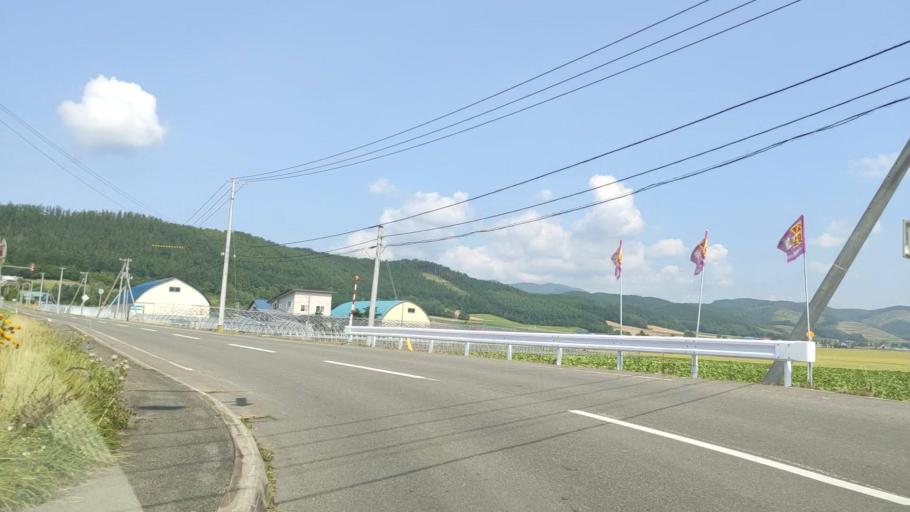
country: JP
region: Hokkaido
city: Shimo-furano
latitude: 43.3929
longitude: 142.3952
